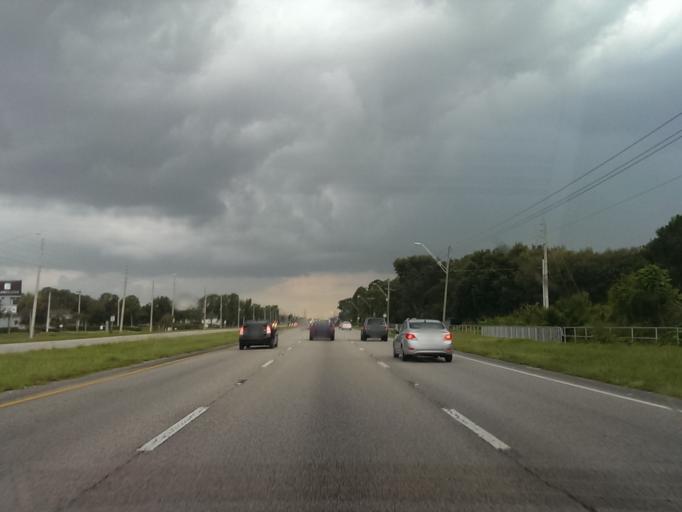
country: US
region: Florida
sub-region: Orange County
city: Orlovista
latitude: 28.5030
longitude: -81.4591
